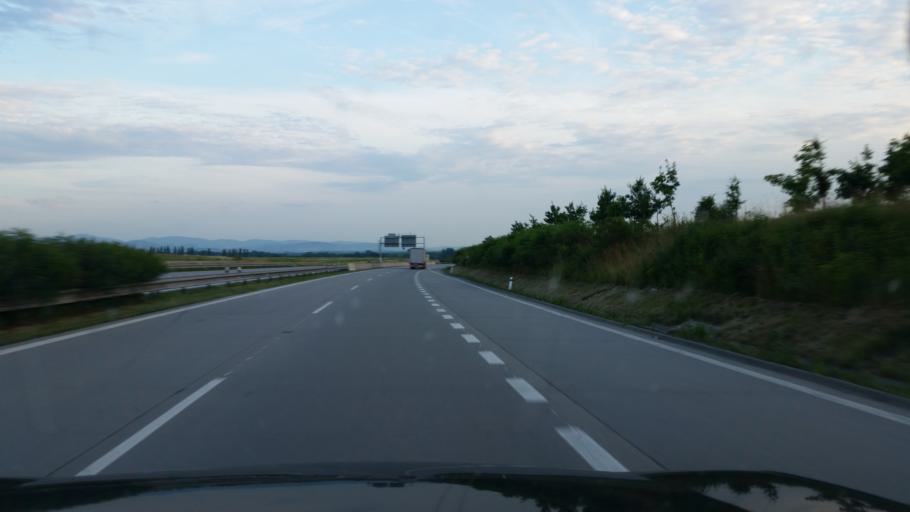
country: CZ
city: Studenka
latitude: 49.7533
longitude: 18.0954
